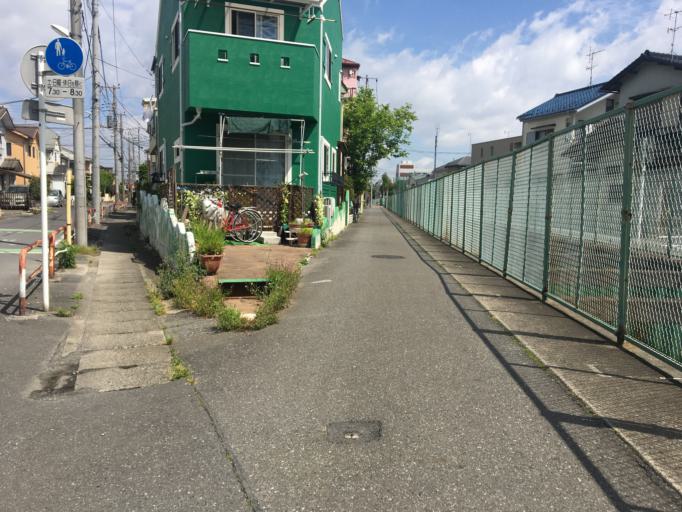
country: JP
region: Saitama
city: Yono
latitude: 35.8759
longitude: 139.6076
